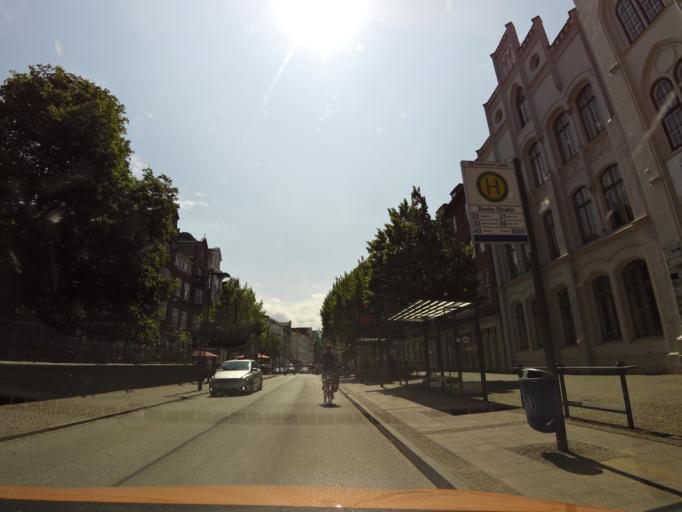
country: DE
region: Schleswig-Holstein
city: Luebeck
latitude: 53.8709
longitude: 10.6883
